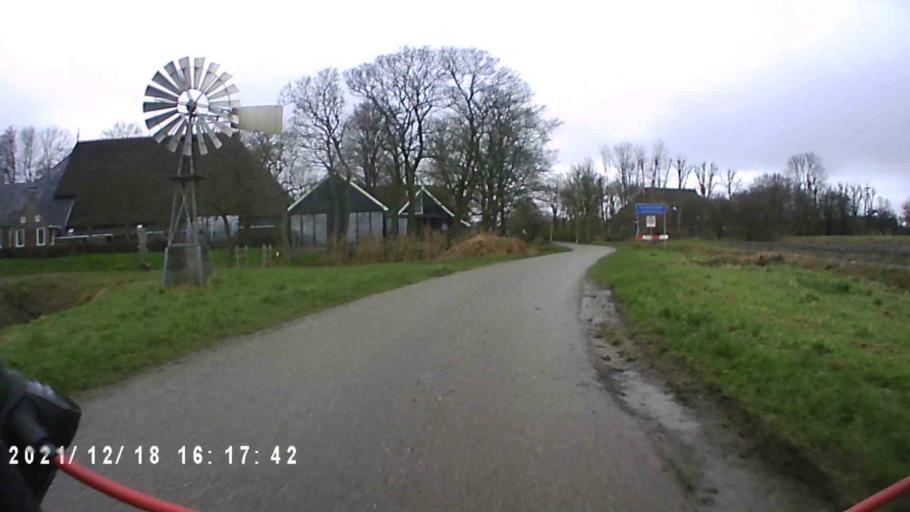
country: NL
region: Friesland
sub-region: Gemeente Dongeradeel
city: Anjum
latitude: 53.3757
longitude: 6.0574
